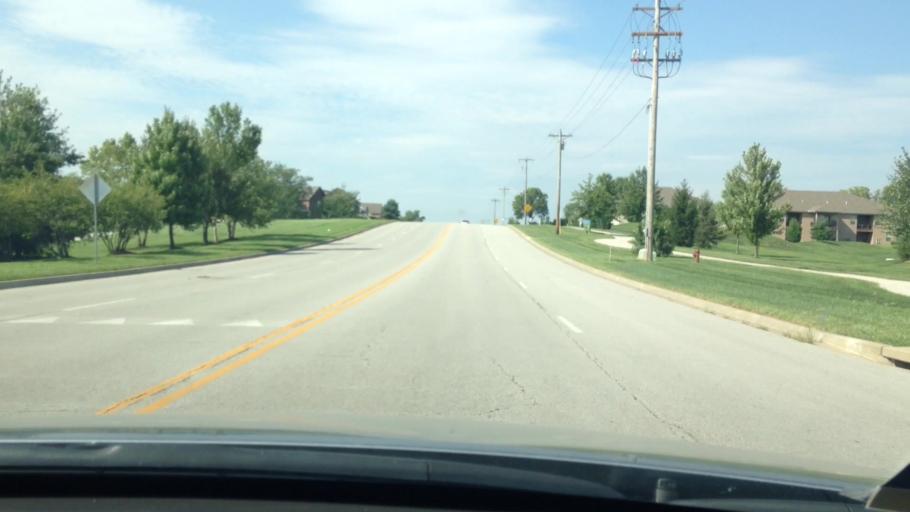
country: US
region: Missouri
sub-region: Platte County
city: Platte City
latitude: 39.3162
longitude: -94.7611
